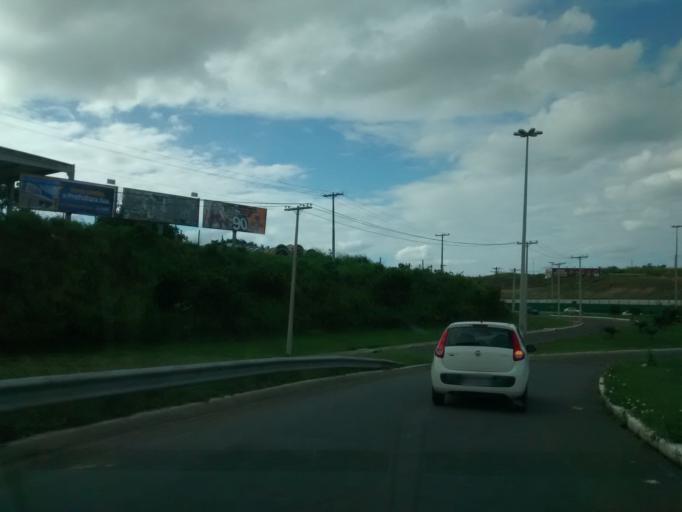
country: BR
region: Bahia
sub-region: Lauro De Freitas
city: Lauro de Freitas
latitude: -12.9202
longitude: -38.3528
